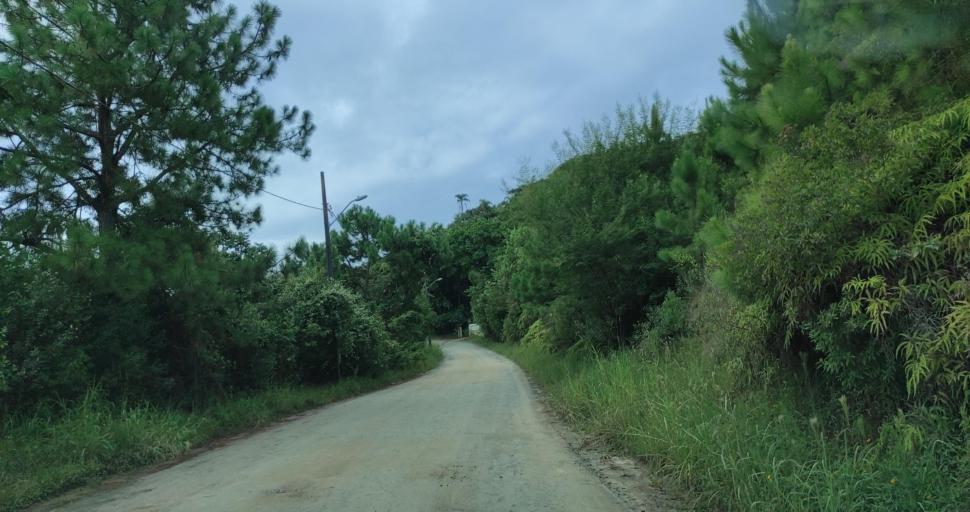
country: BR
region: Santa Catarina
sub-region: Porto Belo
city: Porto Belo
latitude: -27.2159
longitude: -48.5074
